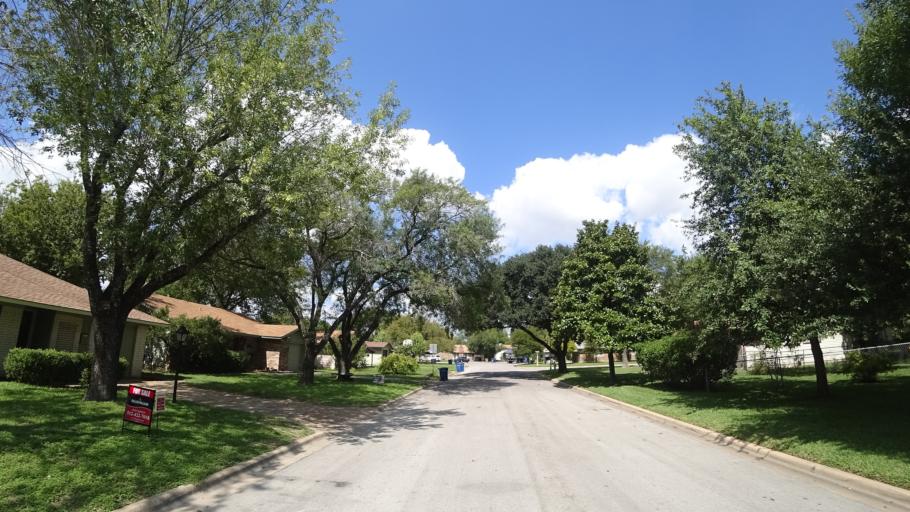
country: US
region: Texas
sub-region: Travis County
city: Wells Branch
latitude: 30.3648
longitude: -97.7231
